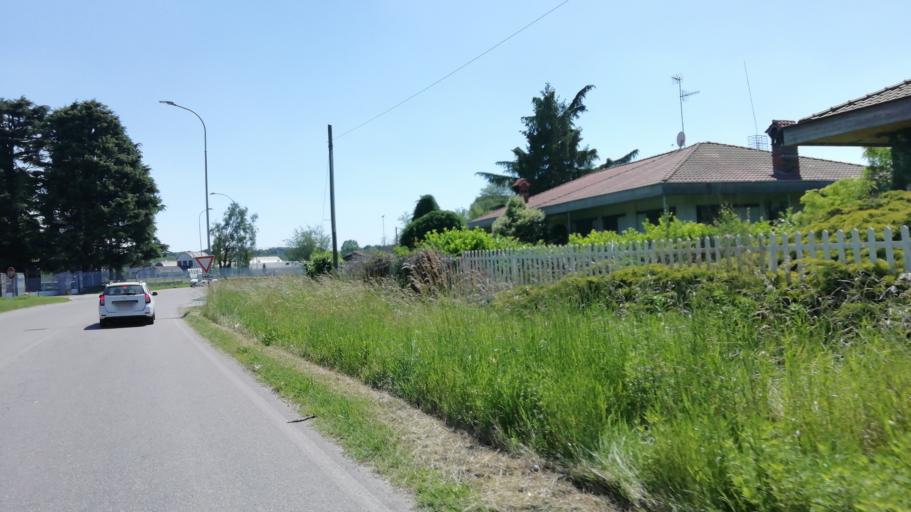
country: IT
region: Lombardy
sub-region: Provincia di Varese
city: Lonate Pozzolo
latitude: 45.5953
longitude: 8.7420
